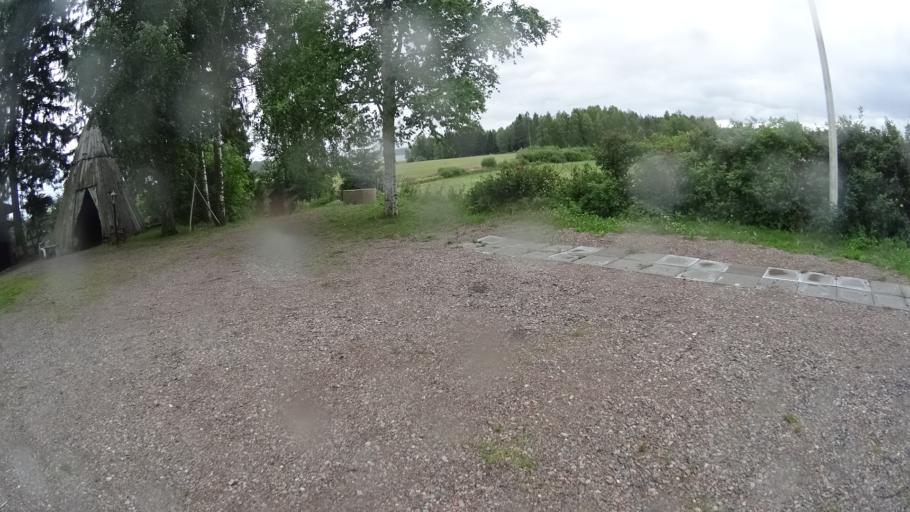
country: FI
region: Uusimaa
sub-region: Helsinki
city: Karkkila
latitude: 60.5835
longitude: 24.3423
